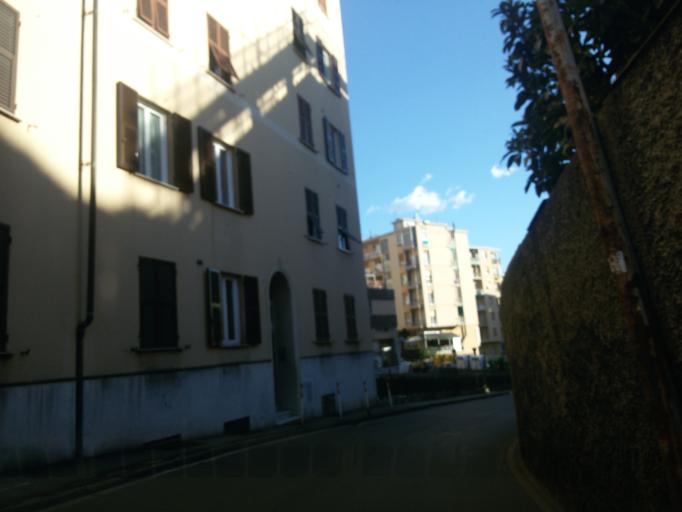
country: IT
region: Liguria
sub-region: Provincia di Genova
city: Bogliasco
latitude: 44.3930
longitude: 8.9988
